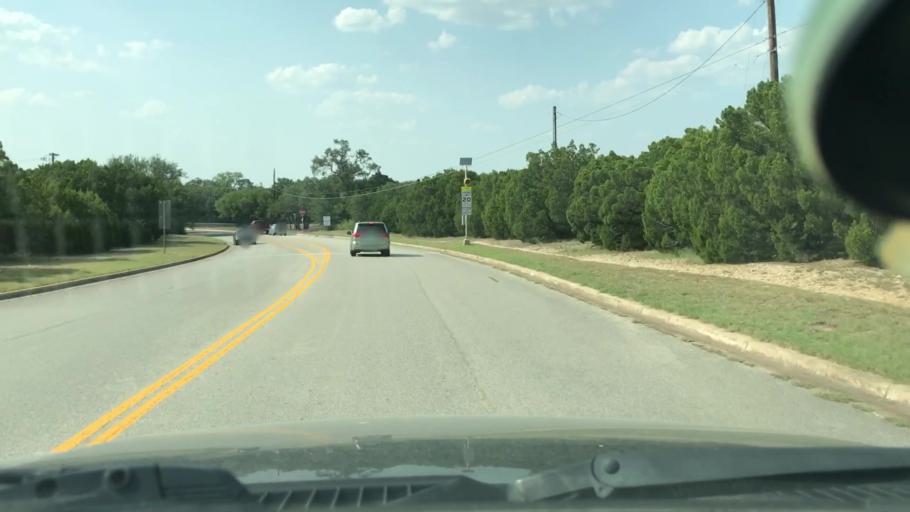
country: US
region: Texas
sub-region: Williamson County
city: Cedar Park
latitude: 30.5386
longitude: -97.8319
